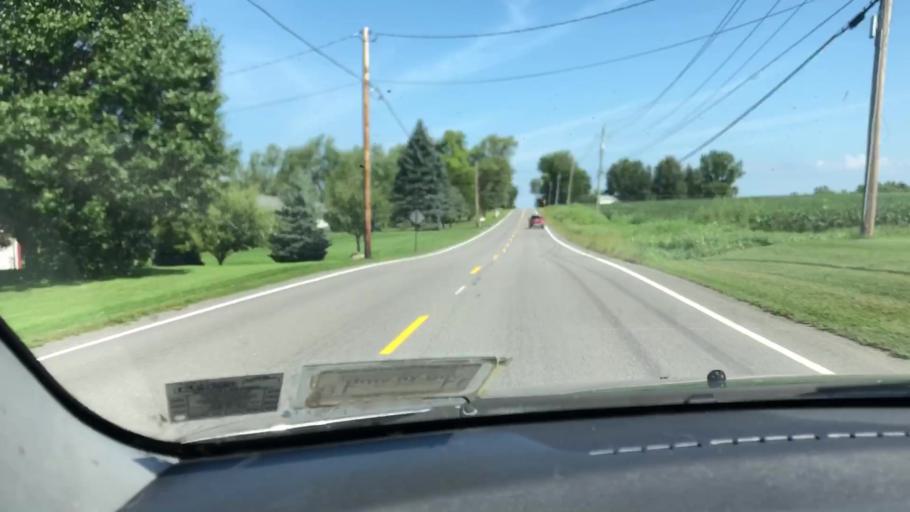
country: US
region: New York
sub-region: Wayne County
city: Macedon
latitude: 43.1049
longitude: -77.3207
